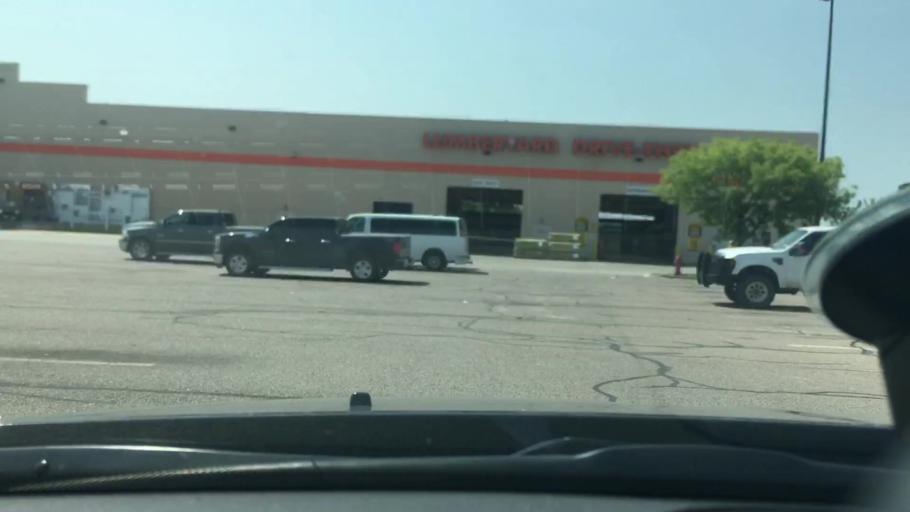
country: US
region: Oklahoma
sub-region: Pontotoc County
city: Ada
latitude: 34.7888
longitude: -96.6721
